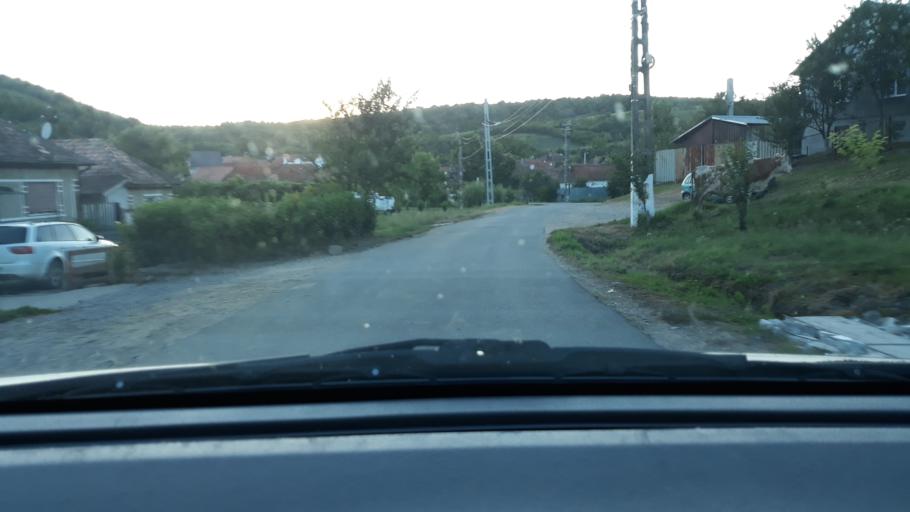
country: RO
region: Bihor
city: Hidiselu de Sus
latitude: 46.9407
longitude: 22.0200
